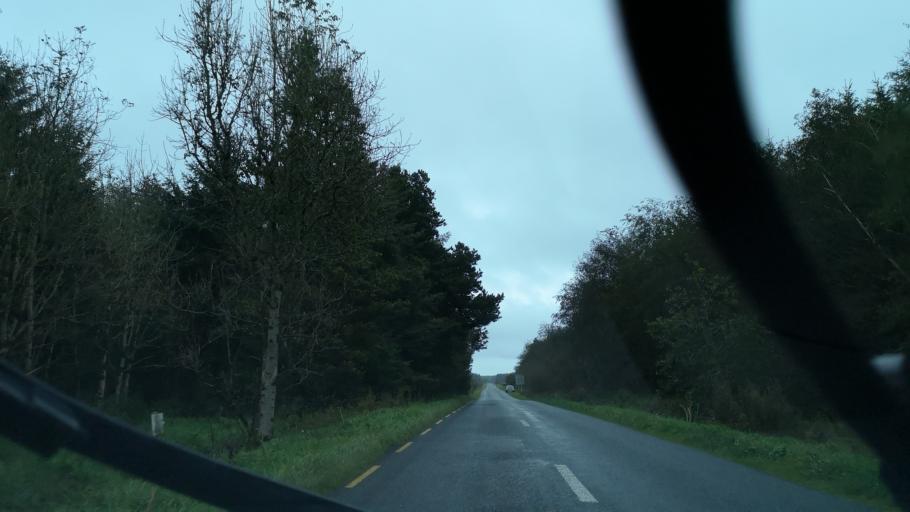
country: IE
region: Connaught
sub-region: Maigh Eo
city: Ballyhaunis
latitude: 53.8123
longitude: -8.6605
